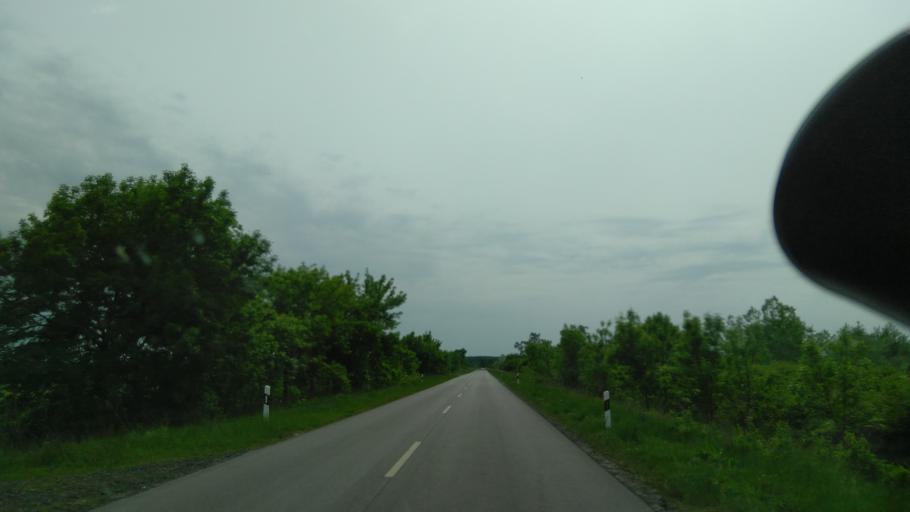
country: HU
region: Bekes
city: Mehkerek
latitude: 46.8332
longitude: 21.4253
